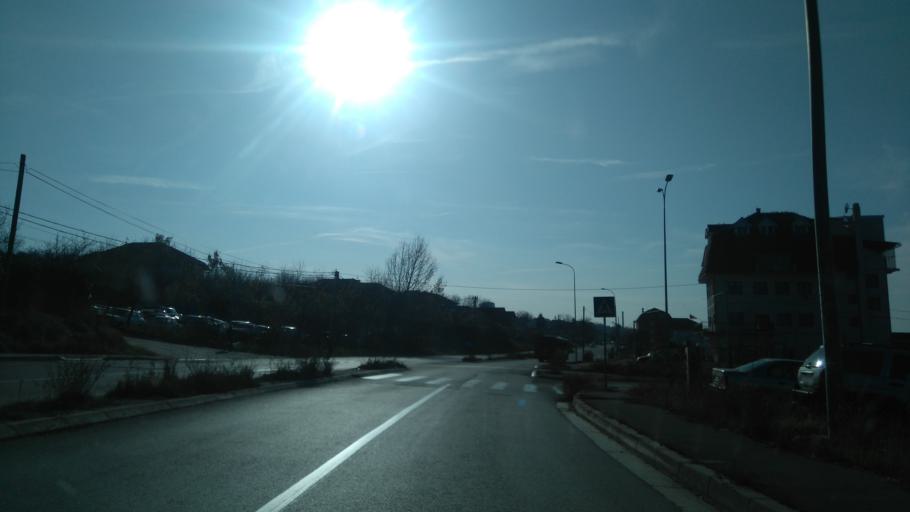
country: RS
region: Central Serbia
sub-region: Belgrade
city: Cukarica
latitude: 44.7419
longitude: 20.3906
